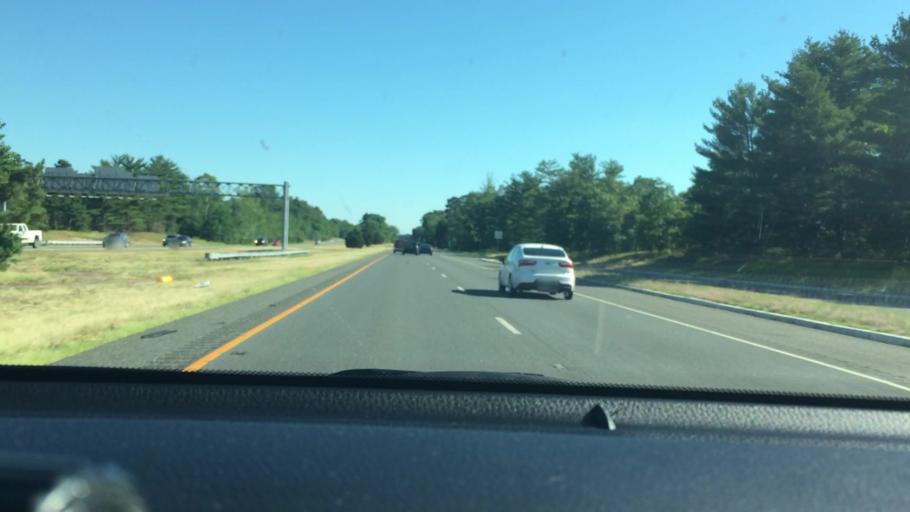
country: US
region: New Jersey
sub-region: Cumberland County
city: Vineland
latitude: 39.4866
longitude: -75.0717
